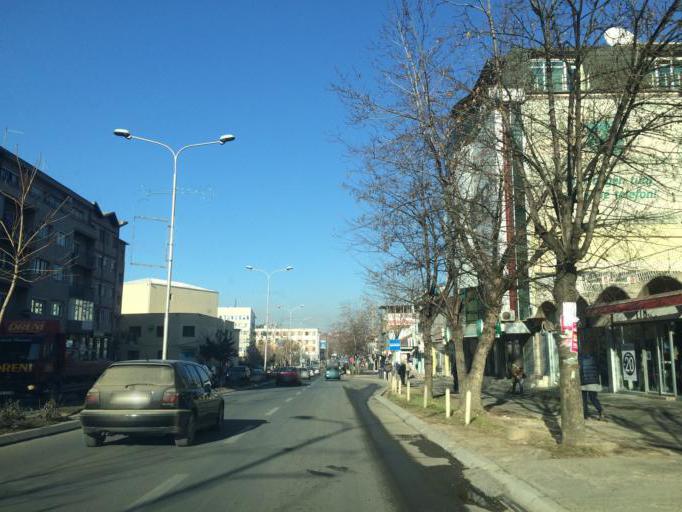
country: XK
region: Pristina
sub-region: Komuna e Prishtines
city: Pristina
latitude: 42.6621
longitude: 21.1651
